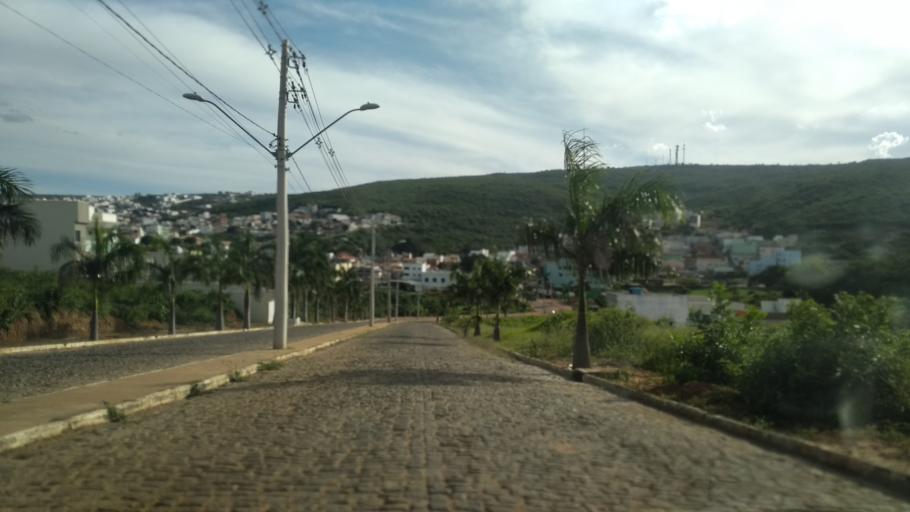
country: BR
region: Bahia
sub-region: Caetite
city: Caetite
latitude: -14.0599
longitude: -42.4955
